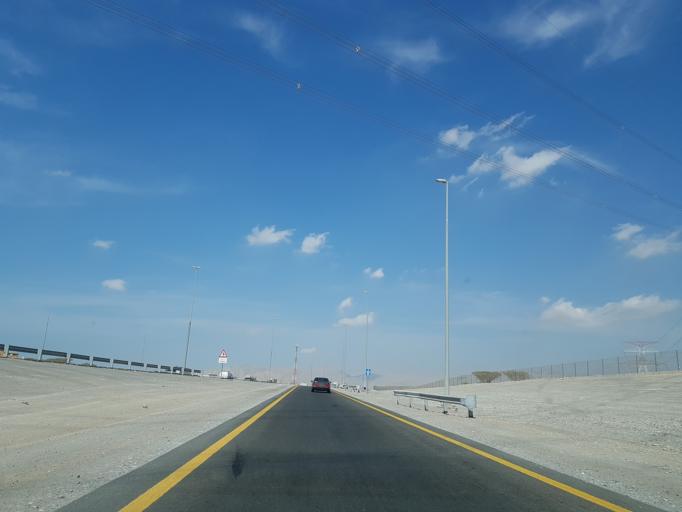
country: AE
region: Ra's al Khaymah
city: Ras al-Khaimah
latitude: 25.7654
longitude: 56.0244
